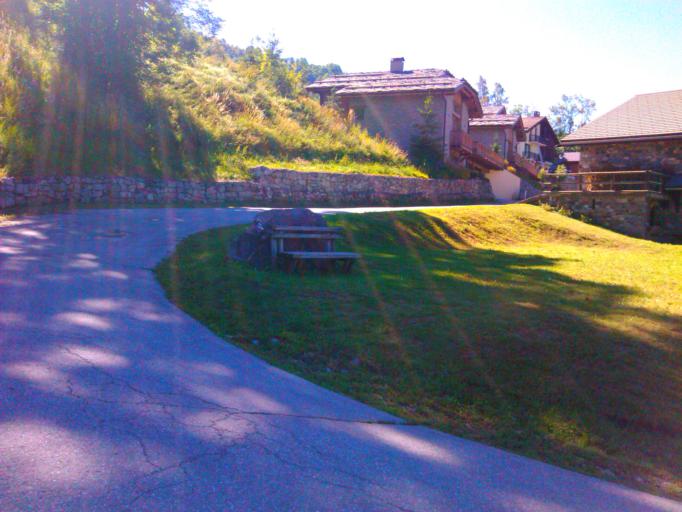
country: FR
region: Rhone-Alpes
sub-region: Departement de la Savoie
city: Saint-Martin-de-Belleville
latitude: 45.3833
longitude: 6.5044
